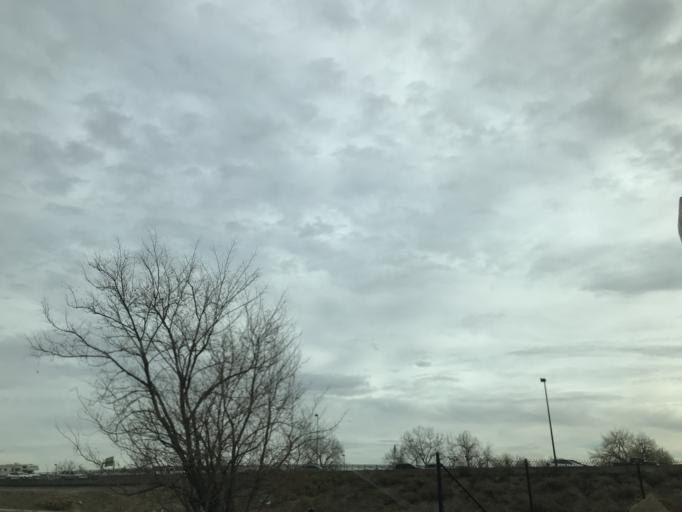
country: US
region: Colorado
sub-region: Adams County
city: Commerce City
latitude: 39.7813
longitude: -104.9037
